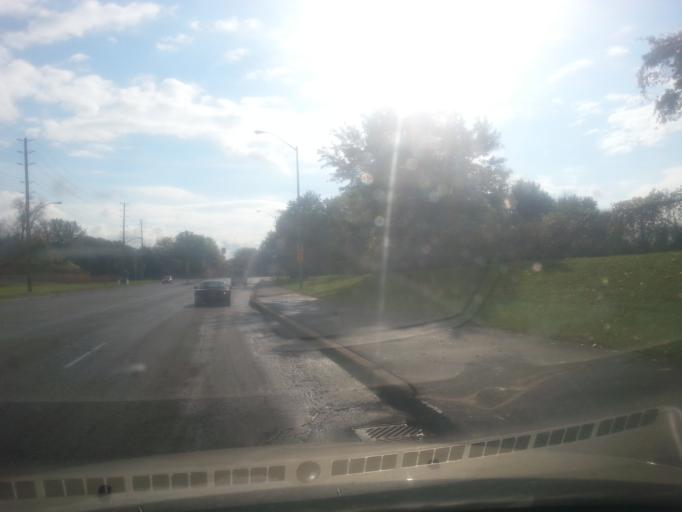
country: CA
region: Ontario
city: Bells Corners
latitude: 45.3433
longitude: -75.8102
